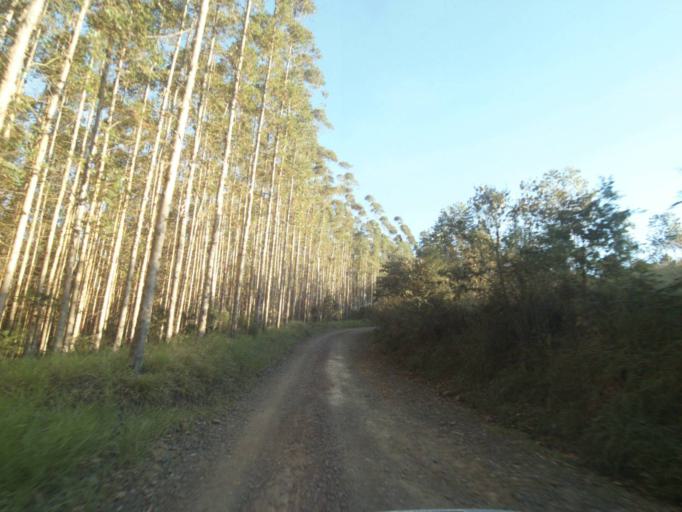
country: BR
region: Parana
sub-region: Telemaco Borba
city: Telemaco Borba
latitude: -24.4908
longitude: -50.5946
